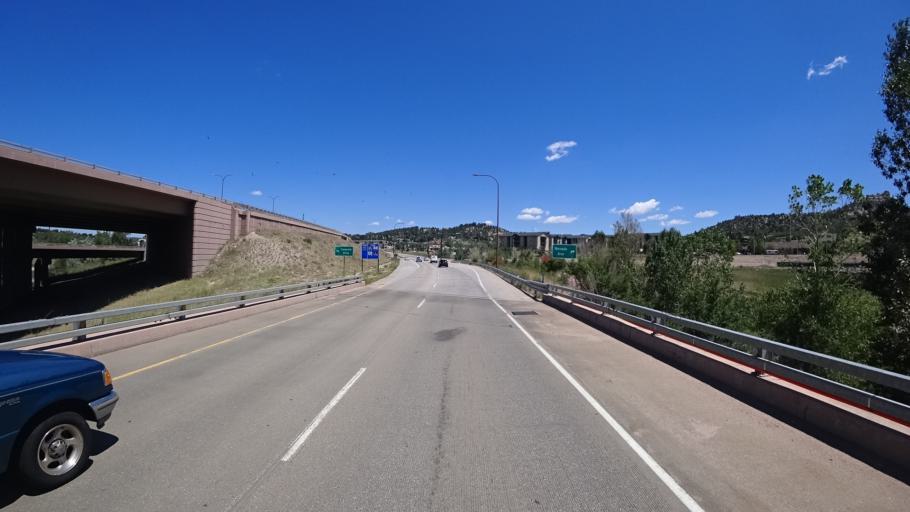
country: US
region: Colorado
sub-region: El Paso County
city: Colorado Springs
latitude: 38.9140
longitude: -104.8180
